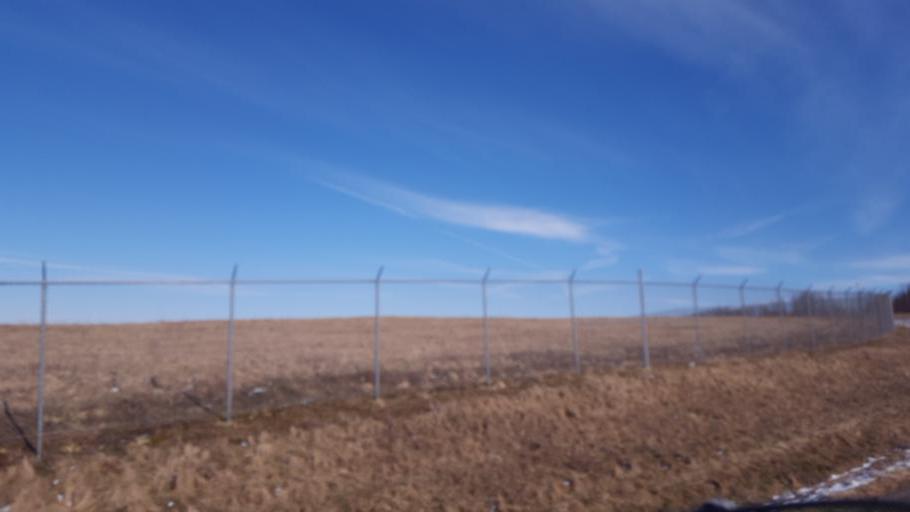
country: US
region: New York
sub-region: Allegany County
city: Wellsville
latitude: 42.1088
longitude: -78.0006
